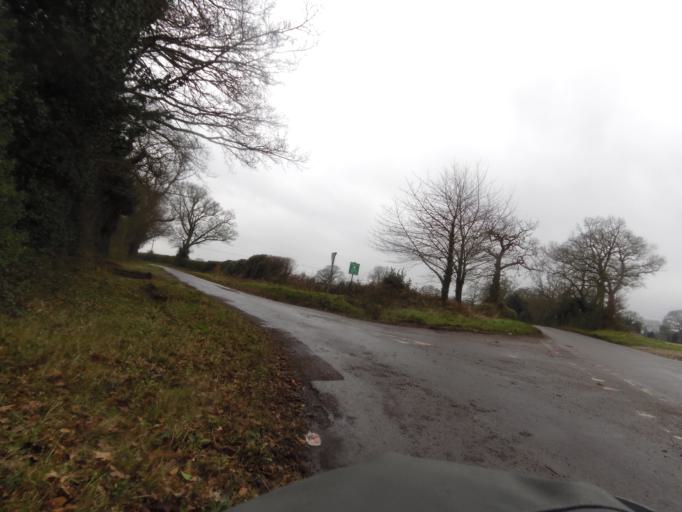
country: GB
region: England
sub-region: Norfolk
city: Briston
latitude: 52.8595
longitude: 1.0642
